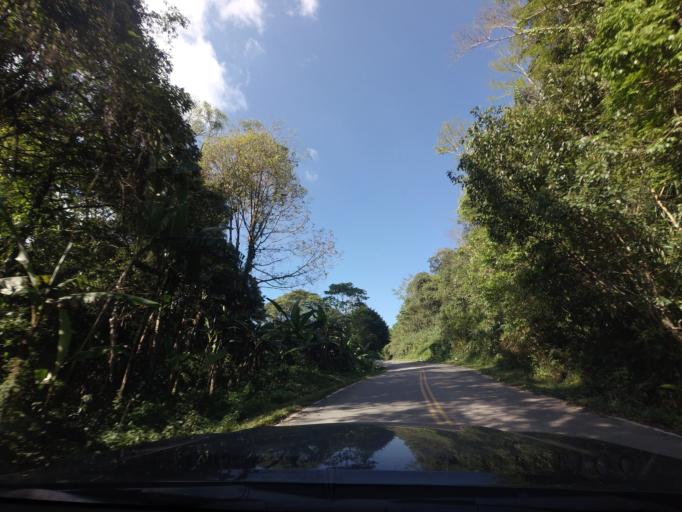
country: TH
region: Phetchabun
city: Lom Kao
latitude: 16.9043
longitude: 101.0744
